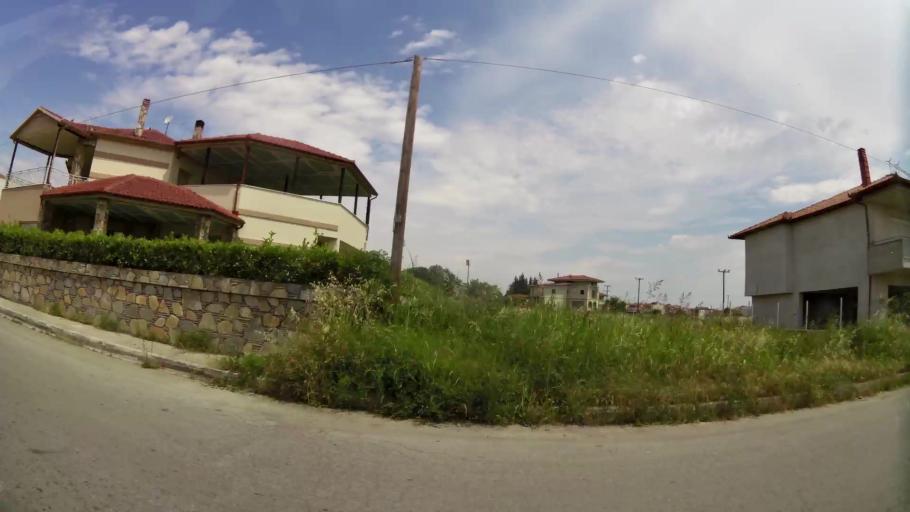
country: GR
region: Central Macedonia
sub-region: Nomos Pierias
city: Katerini
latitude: 40.2585
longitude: 22.5121
